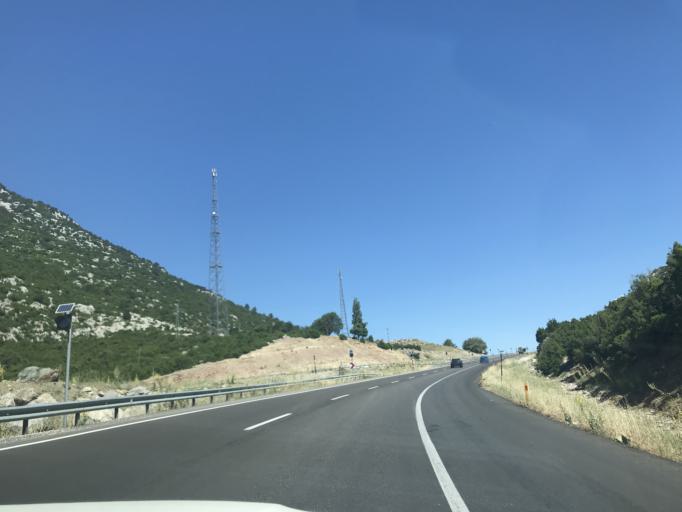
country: TR
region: Antalya
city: Dagbeli
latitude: 37.1658
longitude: 30.4999
